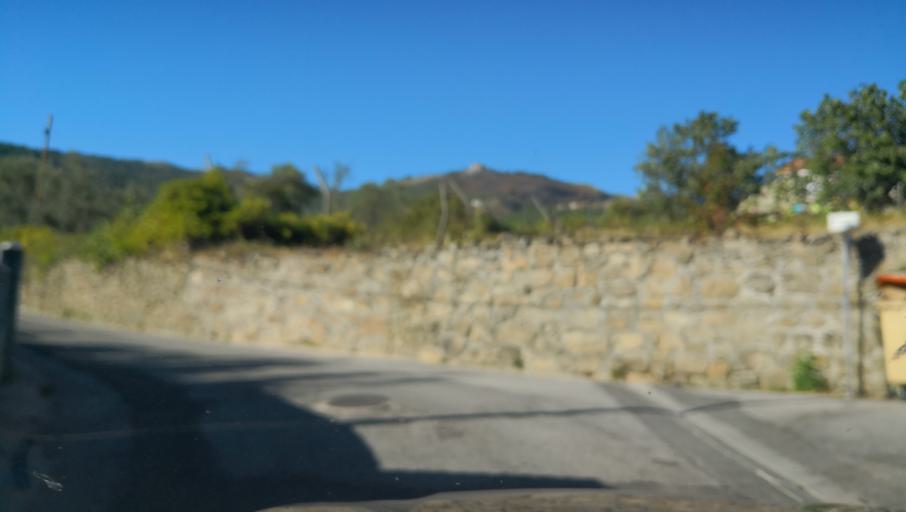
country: PT
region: Vila Real
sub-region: Vila Real
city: Vila Real
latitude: 41.3189
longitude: -7.7672
